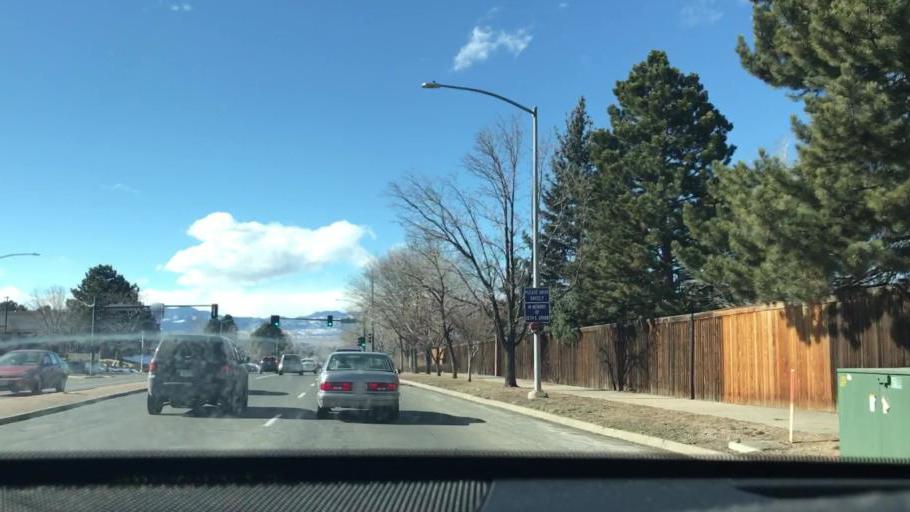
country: US
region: Colorado
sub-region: Adams County
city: Westminster
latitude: 39.8637
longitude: -105.0648
